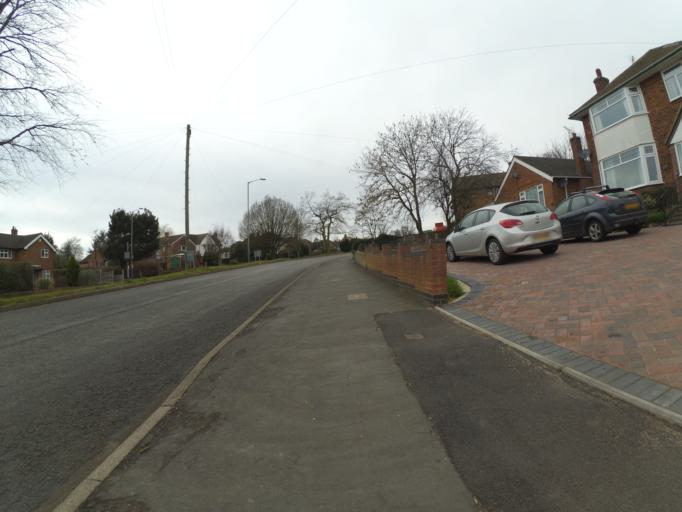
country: GB
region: England
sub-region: Warwickshire
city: Rugby
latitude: 52.3653
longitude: -1.2289
